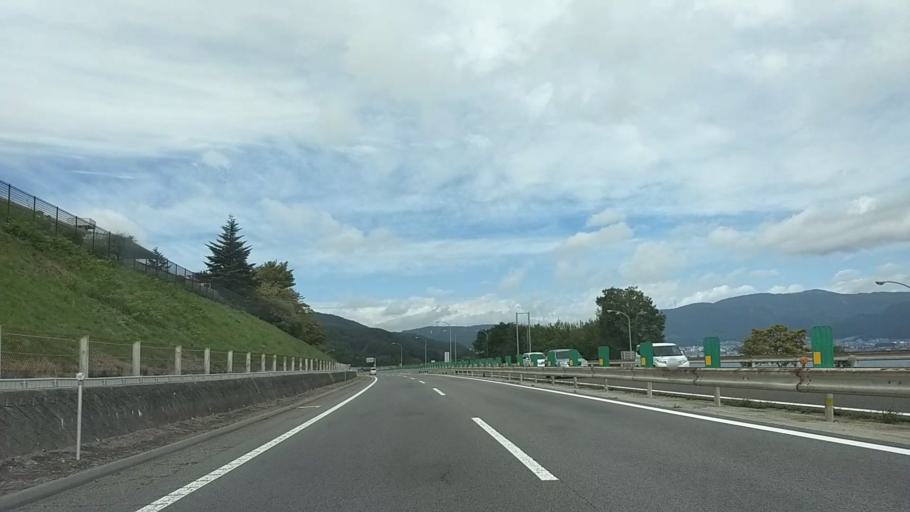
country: JP
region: Nagano
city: Suwa
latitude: 36.0264
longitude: 138.0769
